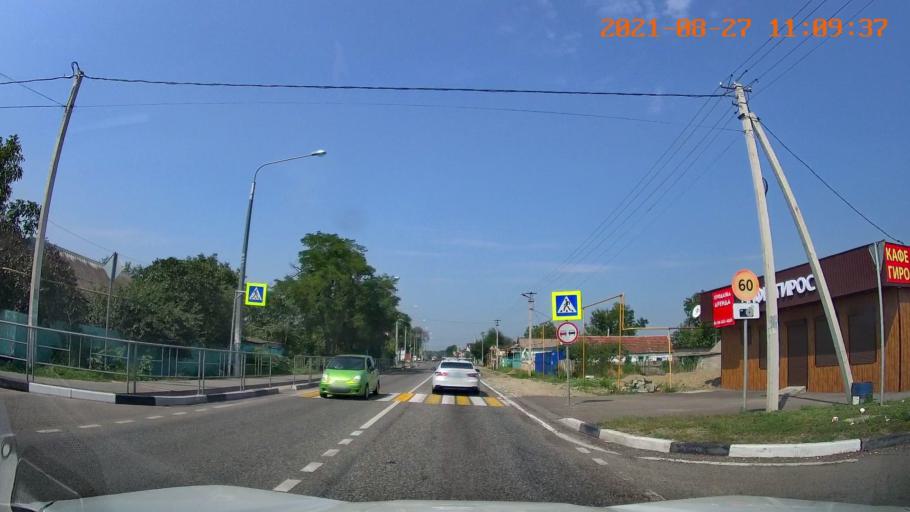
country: RU
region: Stavropol'skiy
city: Ivanovskoye
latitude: 44.5710
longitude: 41.8739
